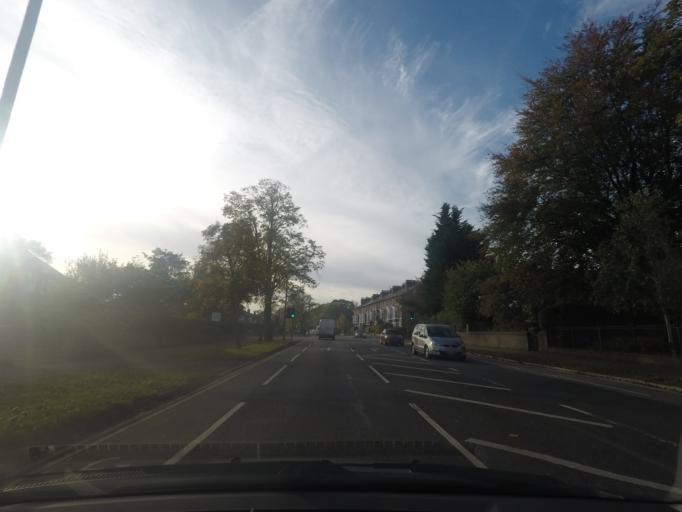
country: GB
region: England
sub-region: City of York
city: Fulford
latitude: 53.9412
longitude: -1.0742
